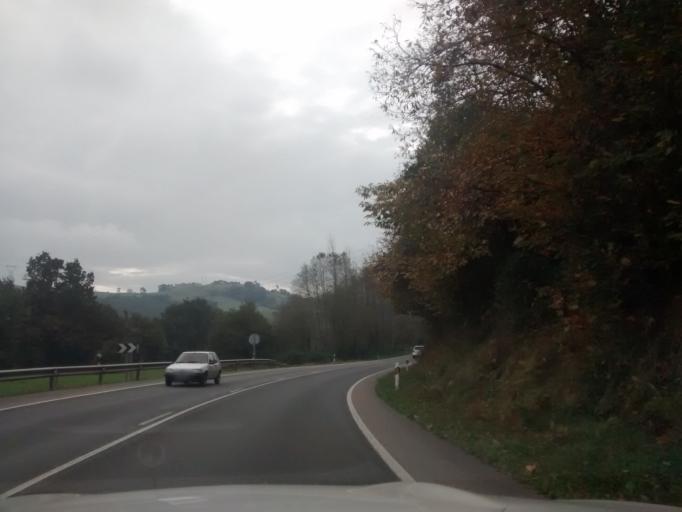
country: ES
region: Cantabria
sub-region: Provincia de Cantabria
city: Puente Viesgo
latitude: 43.3124
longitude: -3.9592
